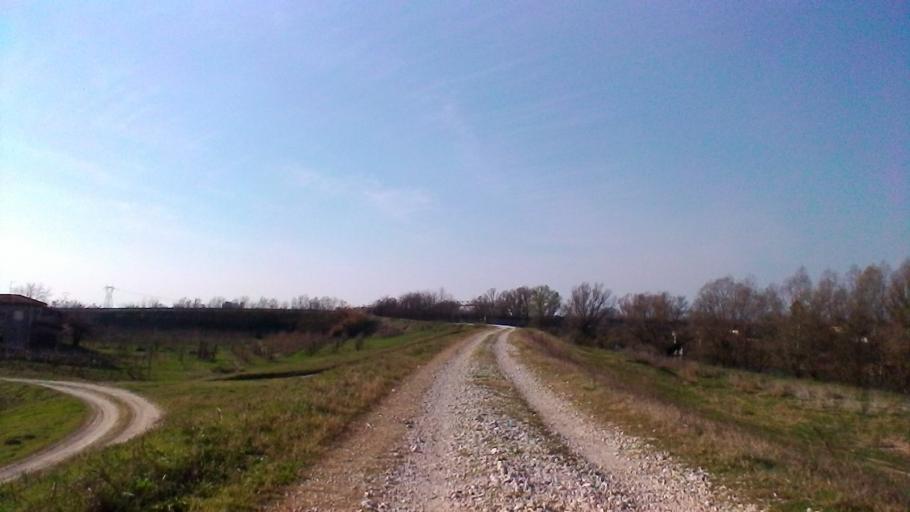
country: IT
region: Veneto
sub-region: Provincia di Verona
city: Belfiore
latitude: 45.3669
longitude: 11.1980
